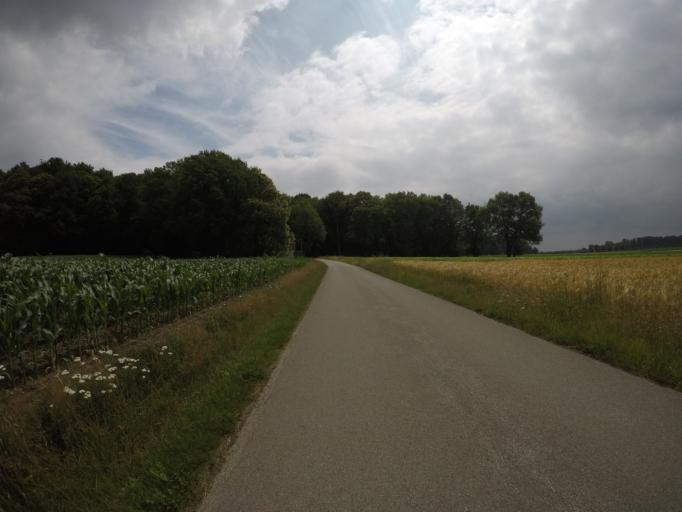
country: DE
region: North Rhine-Westphalia
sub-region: Regierungsbezirk Dusseldorf
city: Hamminkeln
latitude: 51.7343
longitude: 6.6560
